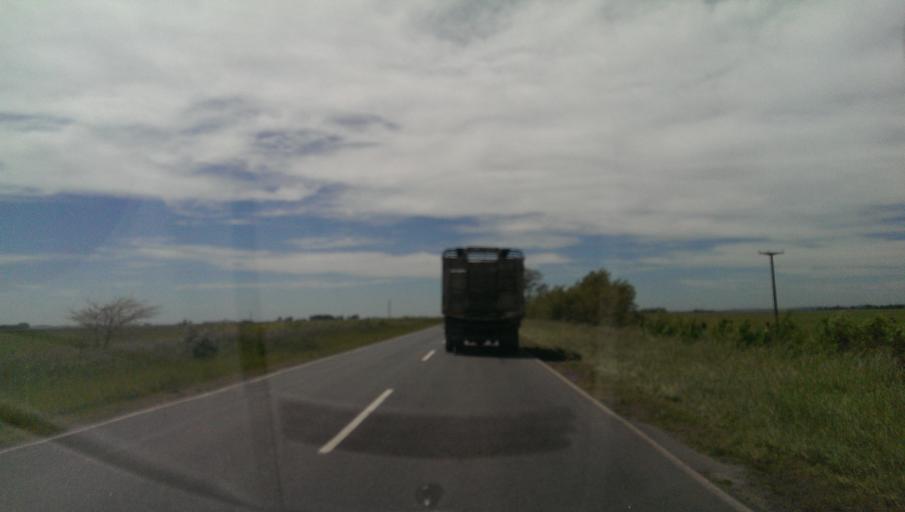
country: AR
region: Buenos Aires
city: Olavarria
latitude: -37.0636
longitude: -60.4627
